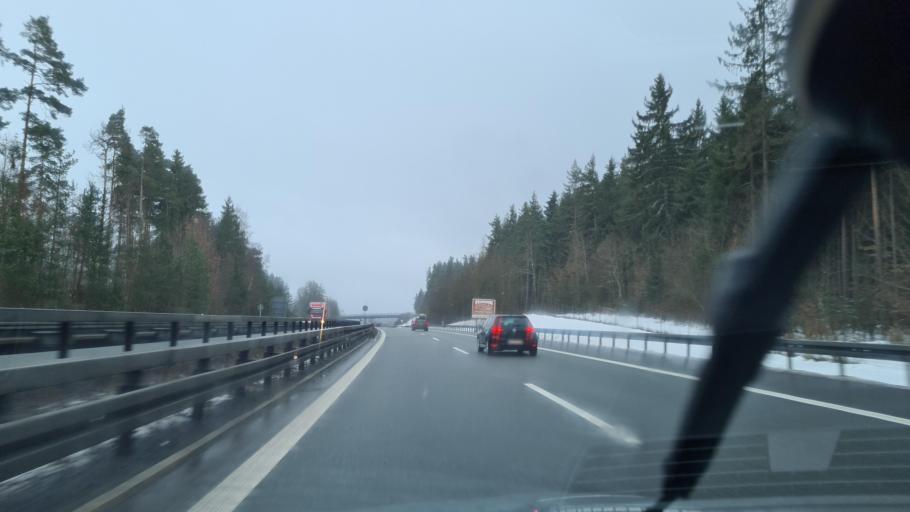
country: DE
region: Bavaria
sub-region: Upper Franconia
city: Thiersheim
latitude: 50.0622
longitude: 12.0980
